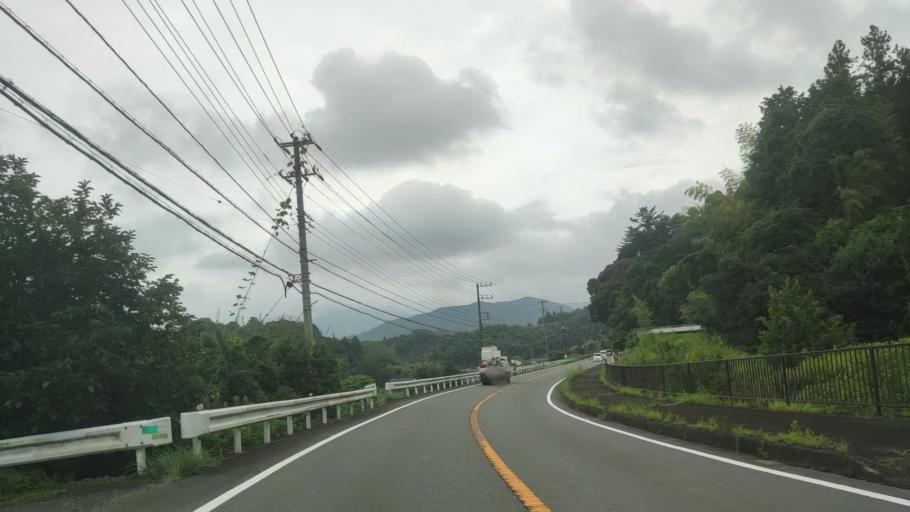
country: JP
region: Shizuoka
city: Fujinomiya
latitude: 35.2044
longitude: 138.5870
